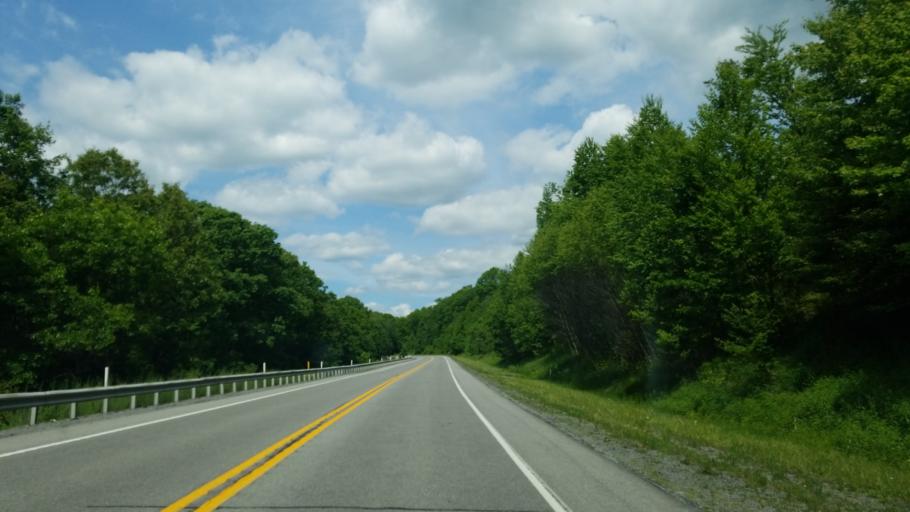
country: US
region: Pennsylvania
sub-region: Clearfield County
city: Clearfield
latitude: 40.9568
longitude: -78.3724
